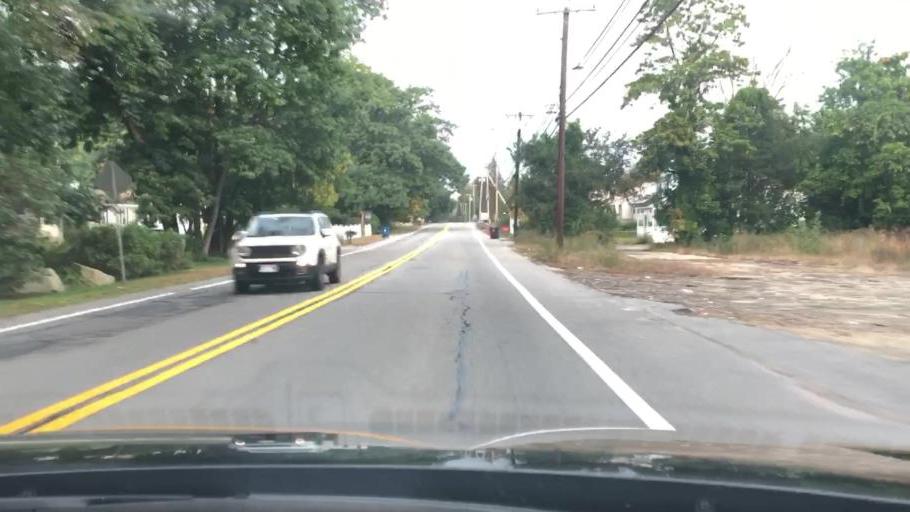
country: US
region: Massachusetts
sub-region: Middlesex County
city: Tyngsboro
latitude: 42.6573
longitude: -71.4033
